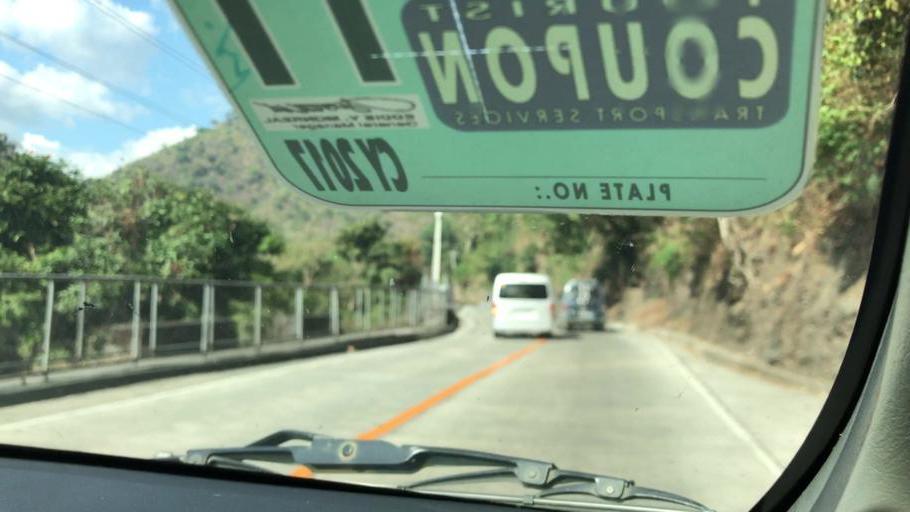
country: PH
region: Cordillera
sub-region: Province of Benguet
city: Tuba
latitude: 16.3116
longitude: 120.6168
